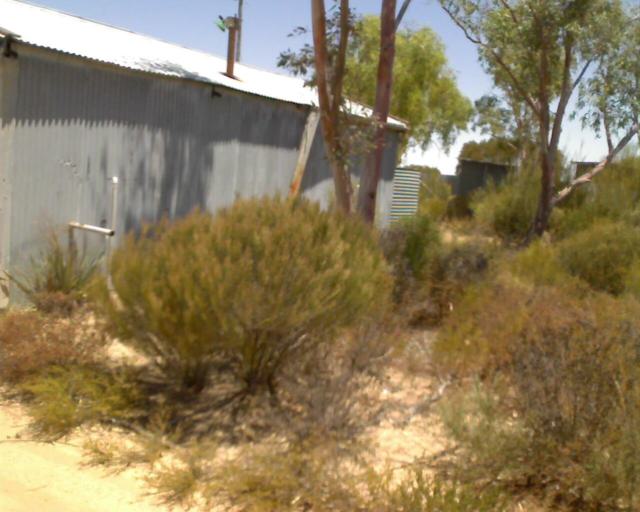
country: AU
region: Western Australia
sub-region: Merredin
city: Merredin
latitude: -30.8224
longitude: 117.8703
